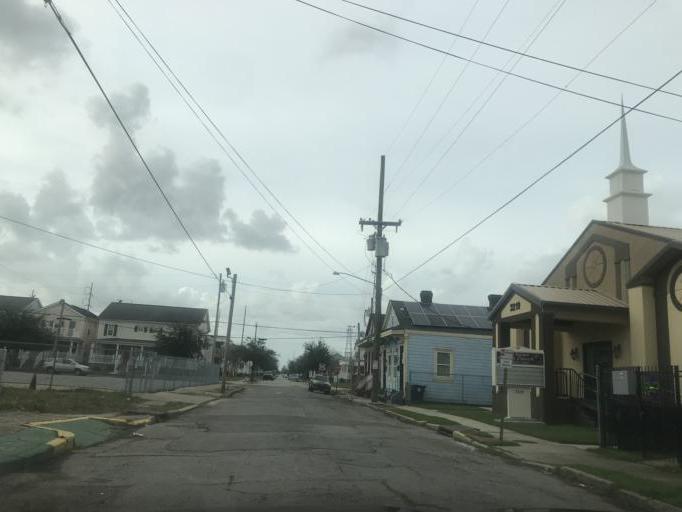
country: US
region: Louisiana
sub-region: Orleans Parish
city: New Orleans
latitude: 29.9484
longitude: -90.0902
